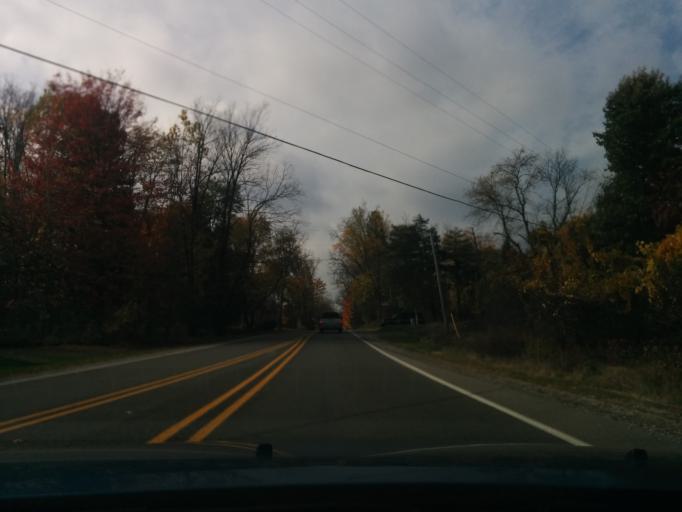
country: US
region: Michigan
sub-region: Washtenaw County
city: Chelsea
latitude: 42.3870
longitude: -84.0016
